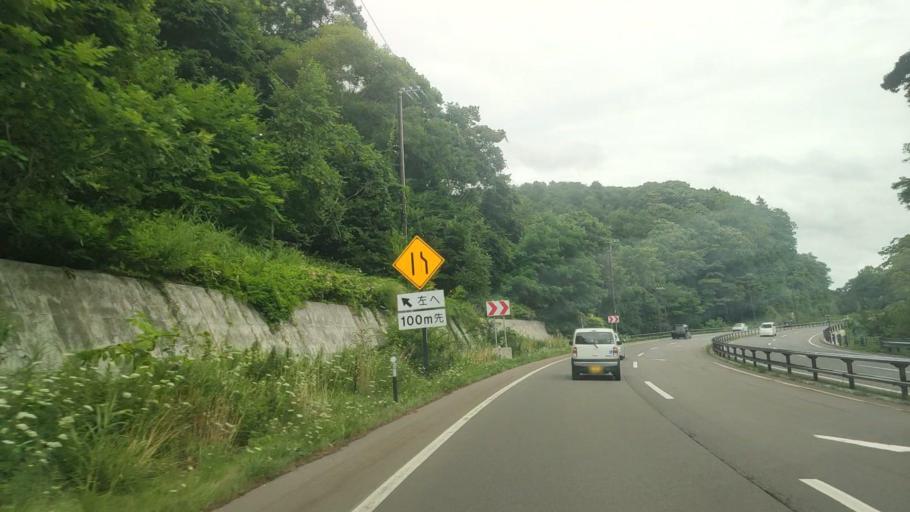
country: JP
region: Hokkaido
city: Nanae
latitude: 41.9627
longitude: 140.6473
